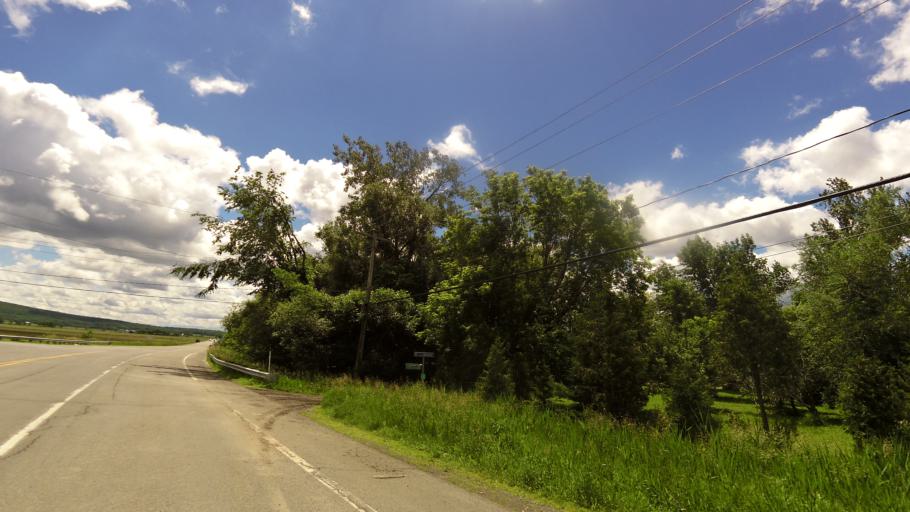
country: CA
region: Quebec
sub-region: Monteregie
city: Hudson
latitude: 45.5294
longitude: -74.1784
